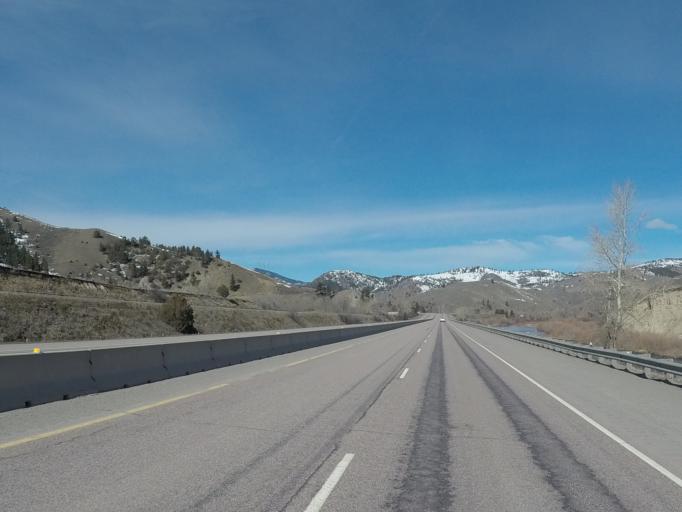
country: US
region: Montana
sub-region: Granite County
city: Philipsburg
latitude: 46.7083
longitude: -113.2590
